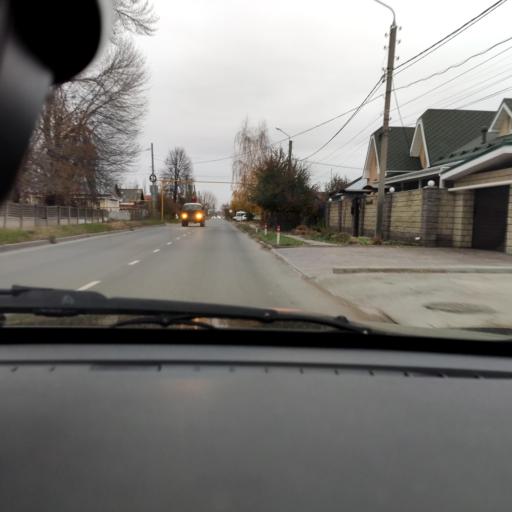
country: RU
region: Samara
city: Tol'yatti
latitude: 53.5333
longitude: 49.4137
